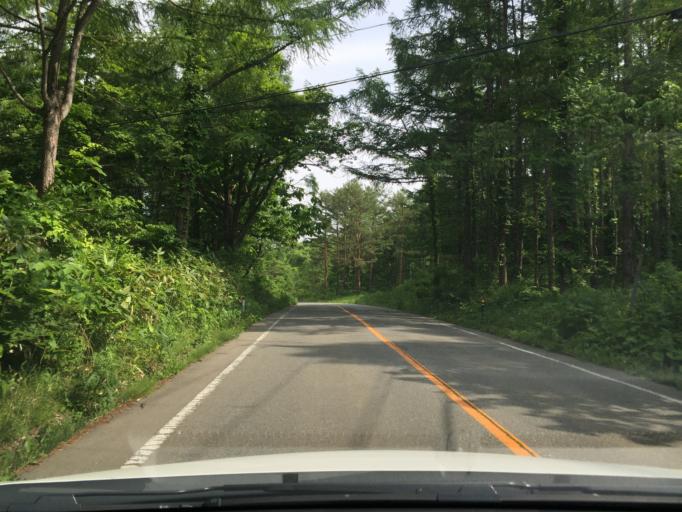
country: JP
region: Fukushima
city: Inawashiro
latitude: 37.6812
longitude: 140.0690
